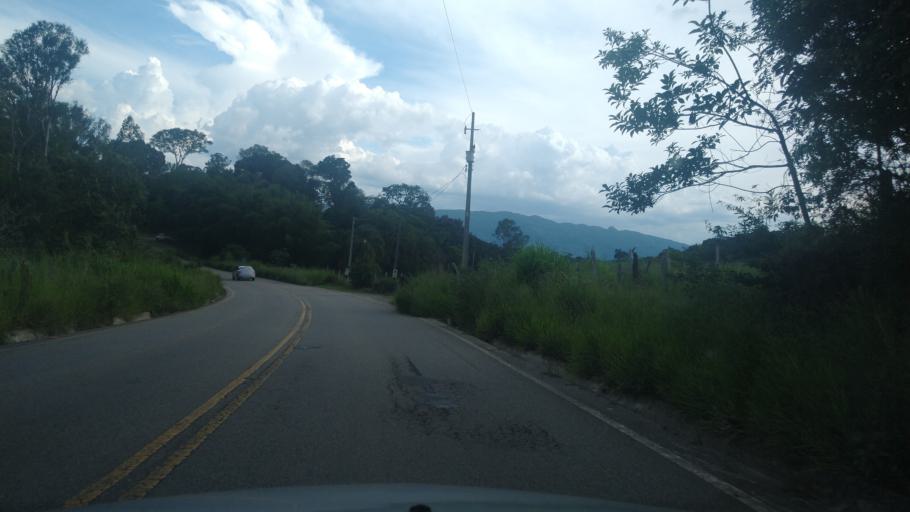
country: BR
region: Minas Gerais
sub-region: Extrema
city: Extrema
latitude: -22.7901
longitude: -46.3191
